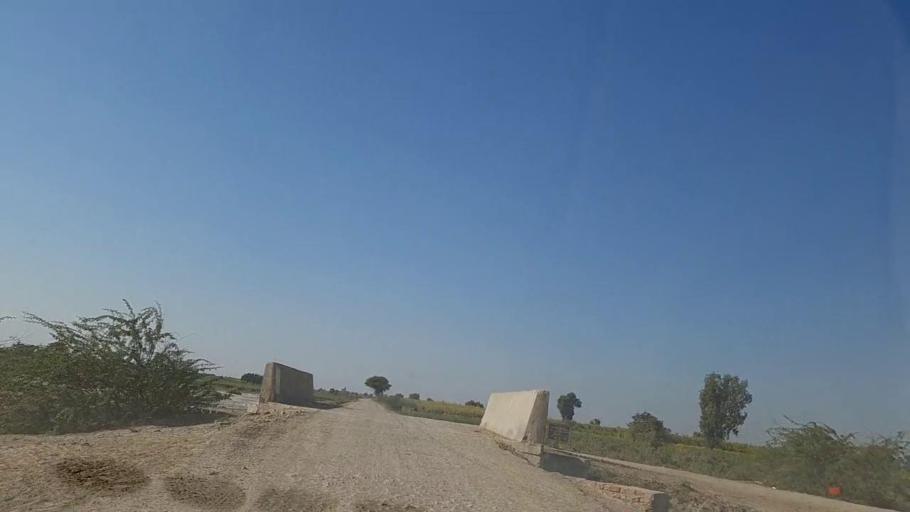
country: PK
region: Sindh
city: Digri
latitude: 25.1830
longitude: 69.0055
